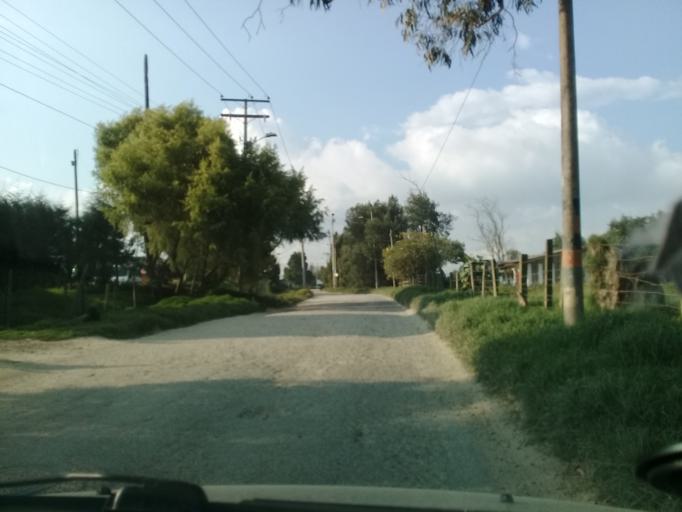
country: CO
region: Cundinamarca
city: Funza
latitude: 4.7418
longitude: -74.2264
